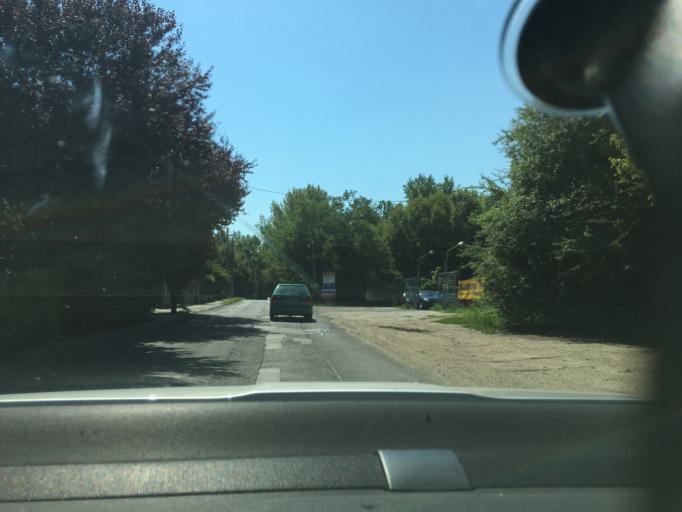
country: HU
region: Budapest
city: Budapest XVI. keruelet
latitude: 47.5034
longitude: 19.1707
